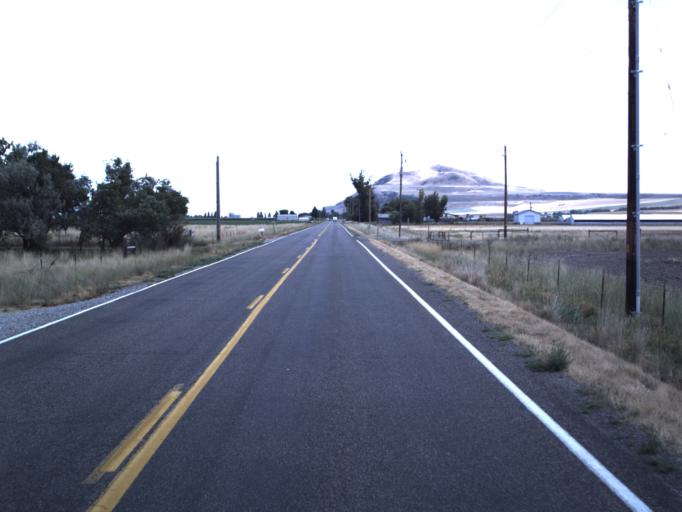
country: US
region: Utah
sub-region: Cache County
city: Lewiston
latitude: 41.9544
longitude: -111.9540
